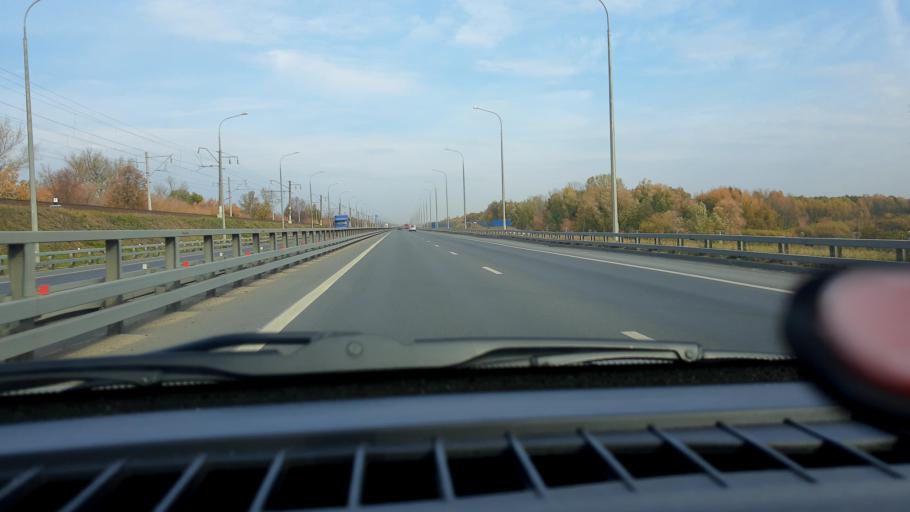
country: RU
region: Nizjnij Novgorod
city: Neklyudovo
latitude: 56.3708
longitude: 43.9455
